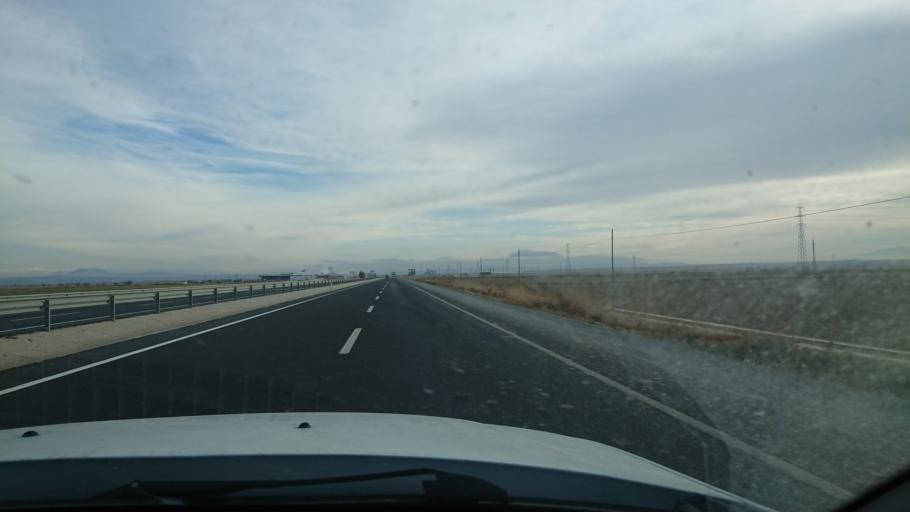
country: TR
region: Aksaray
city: Yesilova
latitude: 38.3115
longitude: 33.8349
